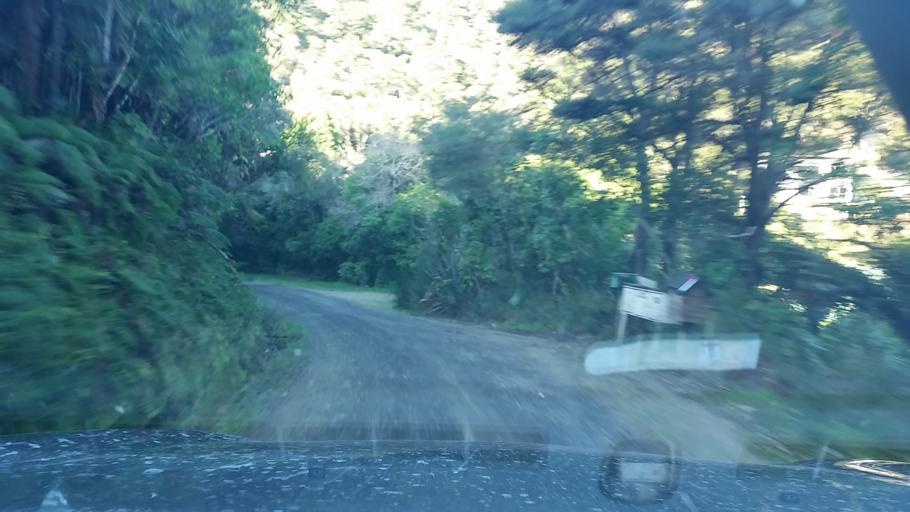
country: NZ
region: Marlborough
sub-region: Marlborough District
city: Picton
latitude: -41.1831
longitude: 173.9750
